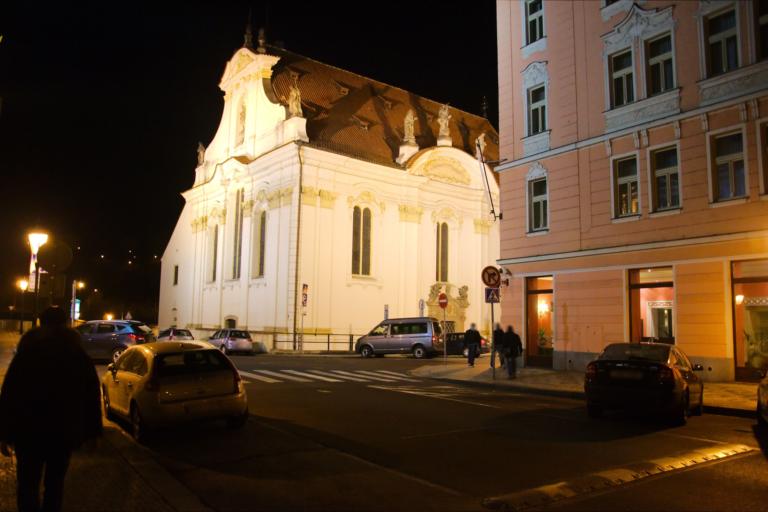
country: CZ
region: Praha
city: Prague
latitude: 50.0912
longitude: 14.4204
